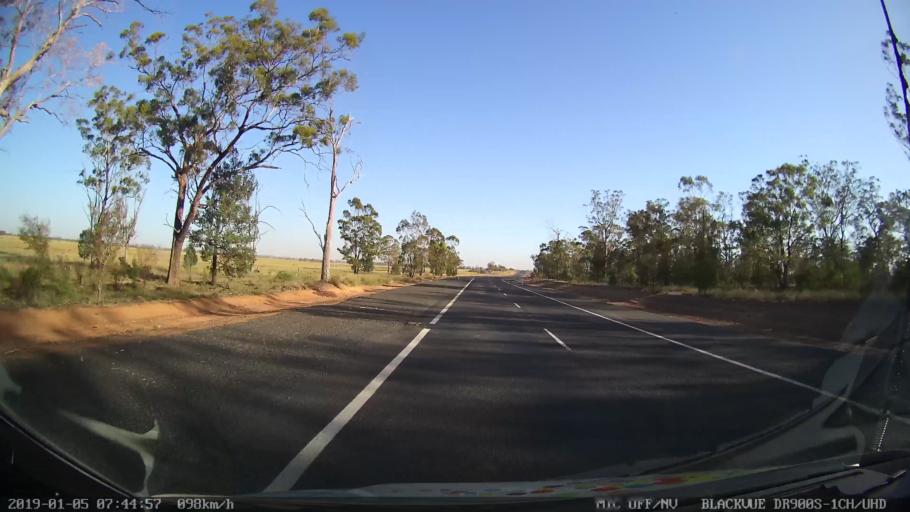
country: AU
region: New South Wales
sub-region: Gilgandra
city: Gilgandra
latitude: -31.8652
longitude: 148.6408
